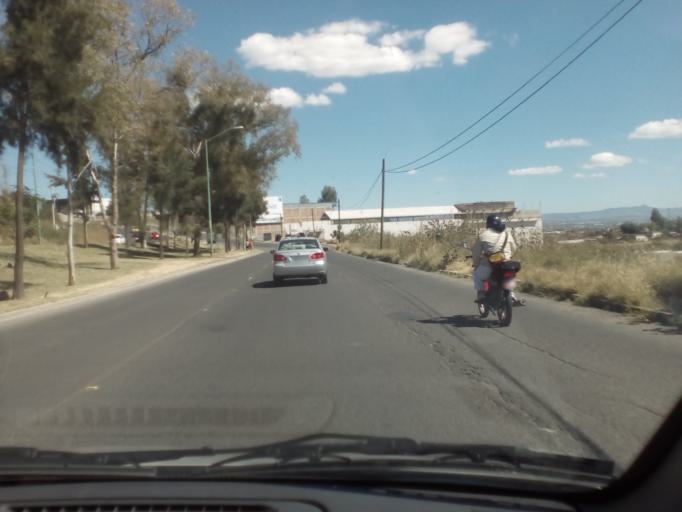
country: MX
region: Guanajuato
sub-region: Leon
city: La Ermita
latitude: 21.1437
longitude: -101.7133
